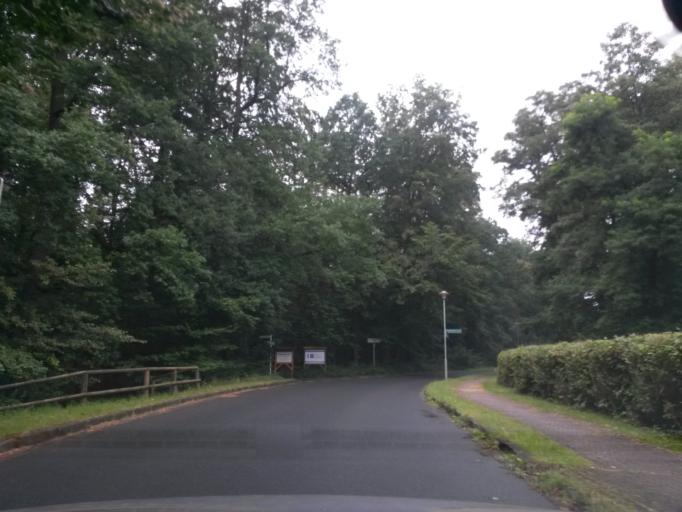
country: DE
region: Brandenburg
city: Chorin
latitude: 52.8999
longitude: 13.8869
